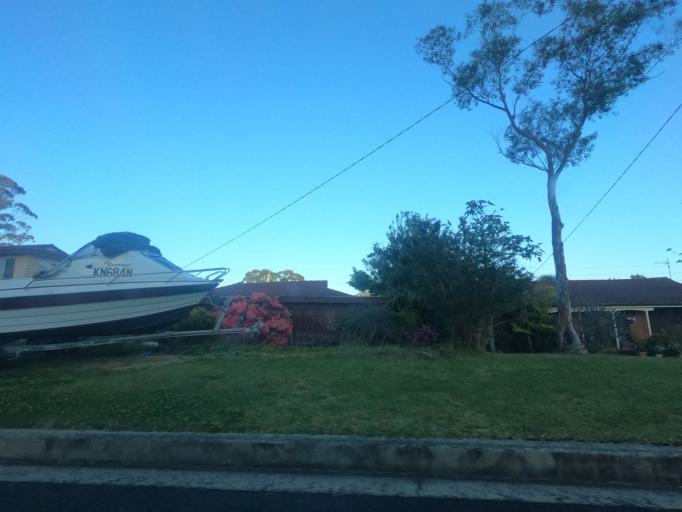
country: AU
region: New South Wales
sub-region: Wollongong
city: Dapto
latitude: -34.5094
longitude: 150.7828
